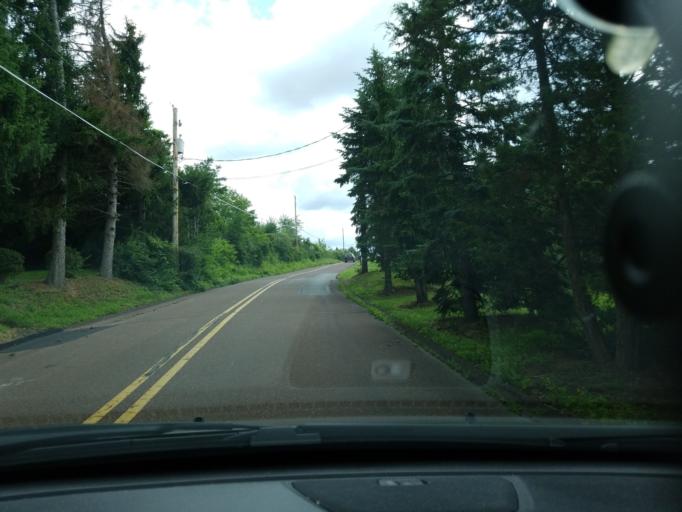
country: US
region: Pennsylvania
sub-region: Northumberland County
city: Elysburg
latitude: 40.8612
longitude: -76.5398
